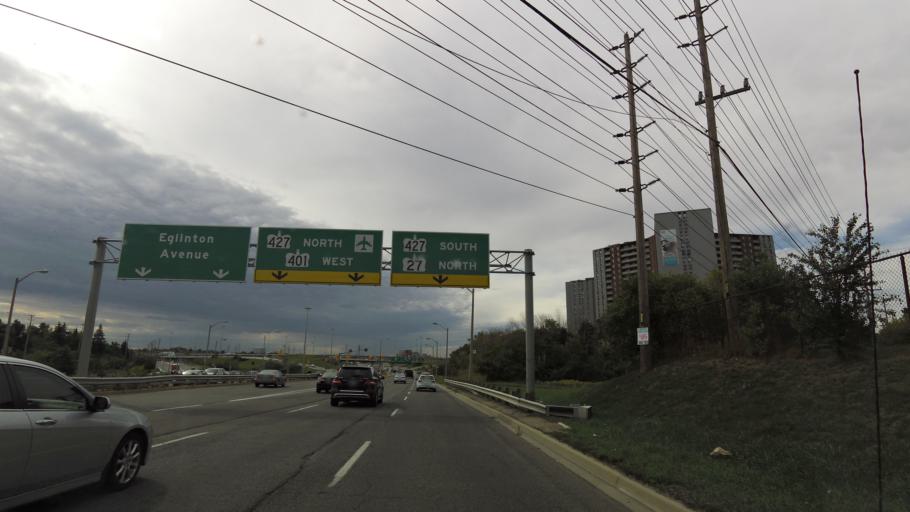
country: CA
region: Ontario
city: Etobicoke
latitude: 43.6743
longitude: -79.5661
